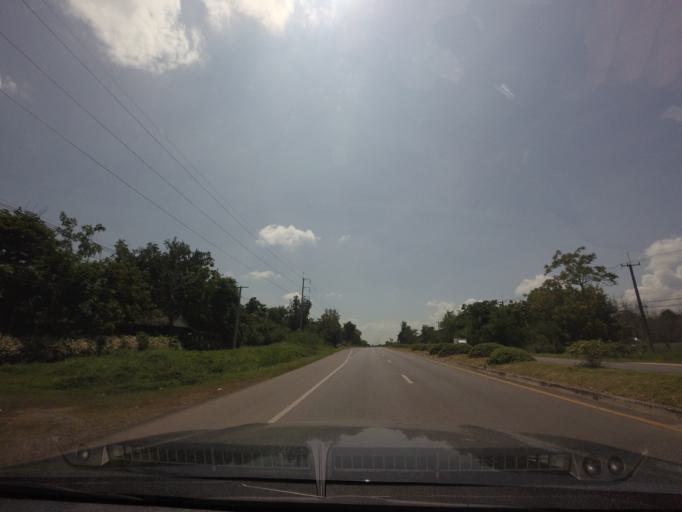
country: TH
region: Phetchabun
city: Lom Sak
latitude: 16.6761
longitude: 101.1611
